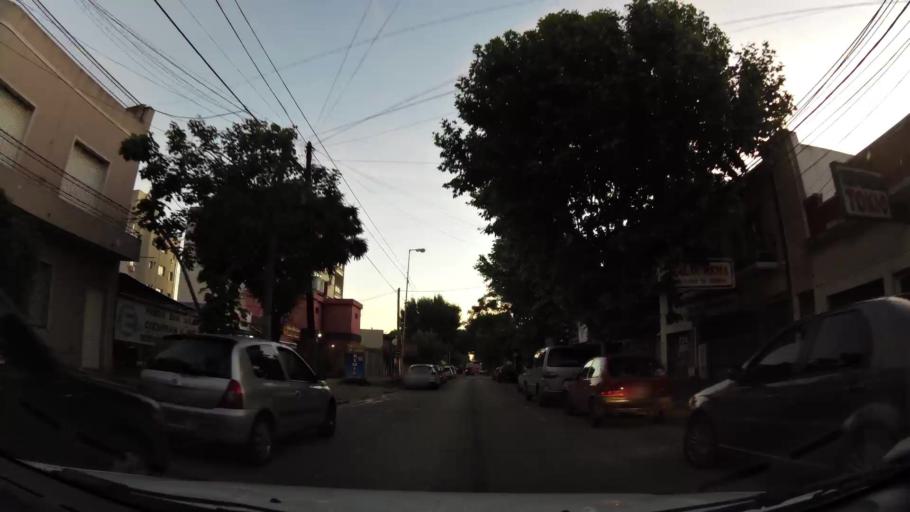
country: AR
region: Buenos Aires
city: Ituzaingo
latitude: -34.6545
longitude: -58.6432
